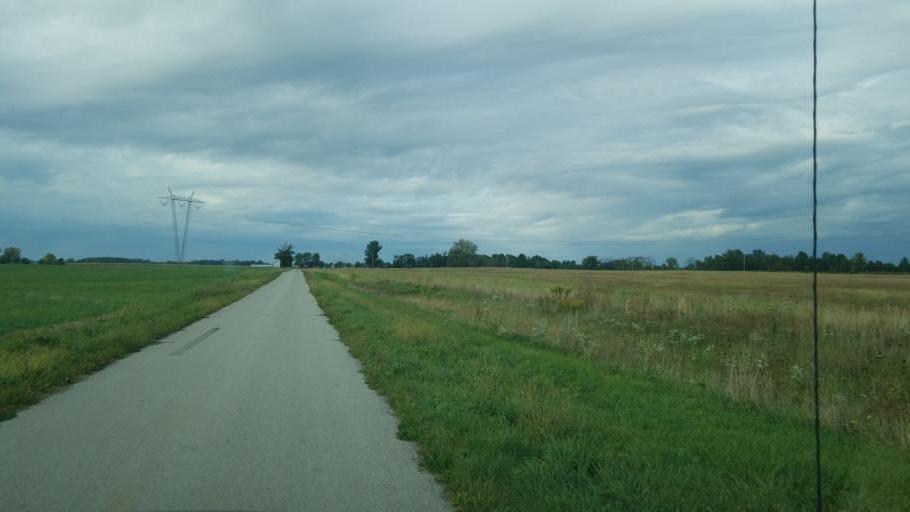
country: US
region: Ohio
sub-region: Wyandot County
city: Upper Sandusky
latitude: 40.9020
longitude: -83.1510
